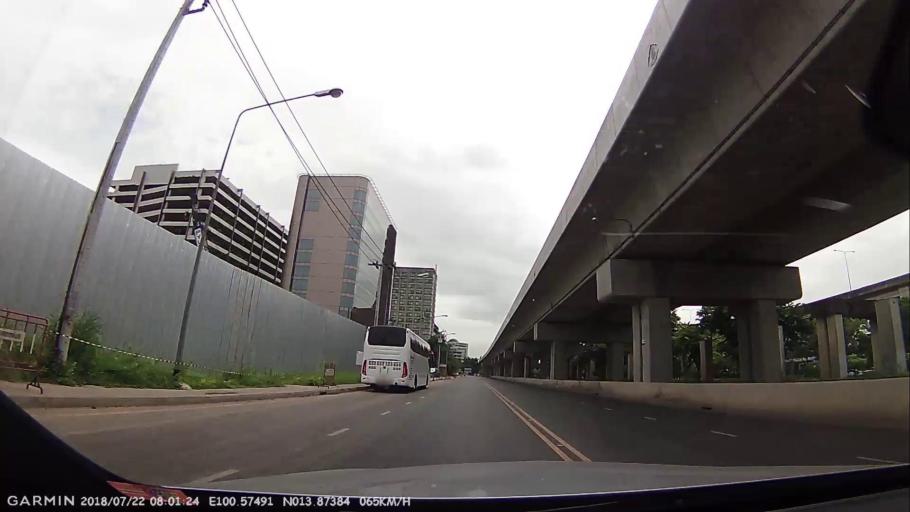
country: TH
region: Bangkok
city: Lak Si
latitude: 13.8740
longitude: 100.5750
